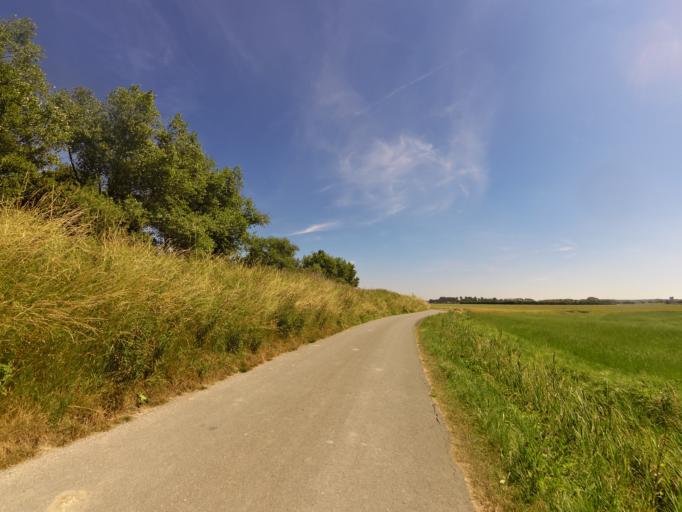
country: NL
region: Zeeland
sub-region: Gemeente Sluis
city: Sluis
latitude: 51.3331
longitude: 3.3670
